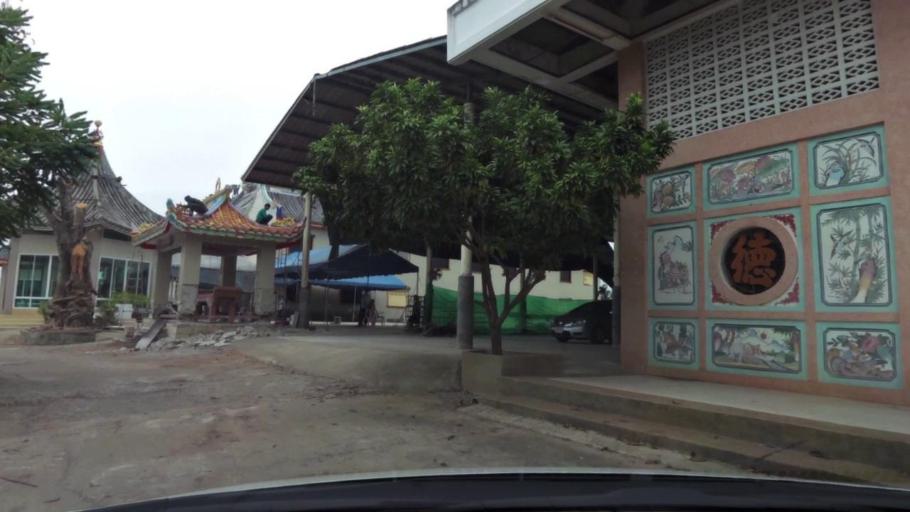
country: TH
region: Samut Sakhon
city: Ban Phaeo
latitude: 13.5984
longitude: 100.0283
